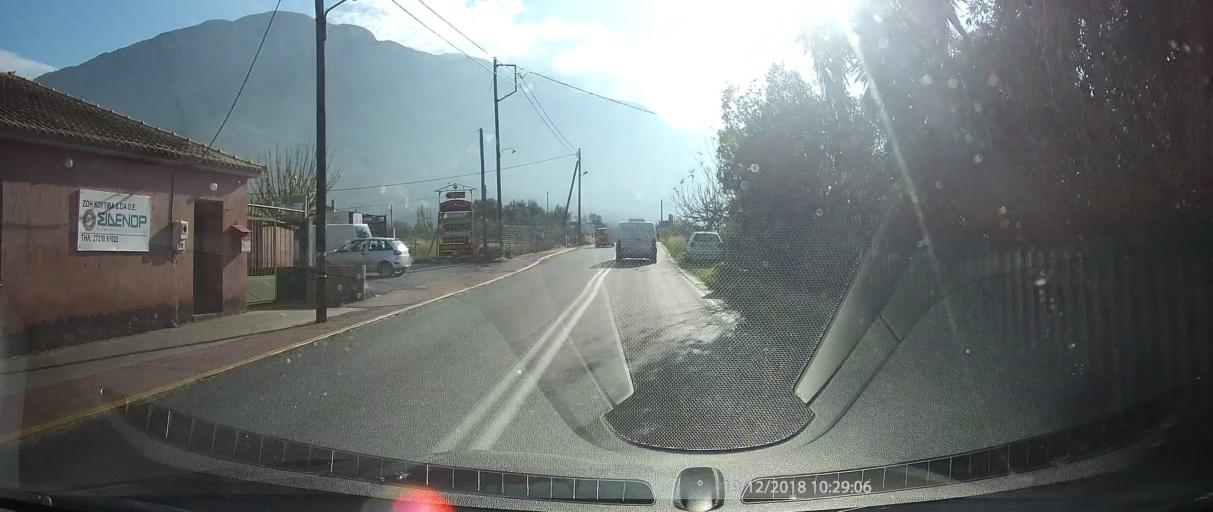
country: GR
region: Peloponnese
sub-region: Nomos Messinias
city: Paralia Vergas
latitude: 37.0244
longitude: 22.1458
